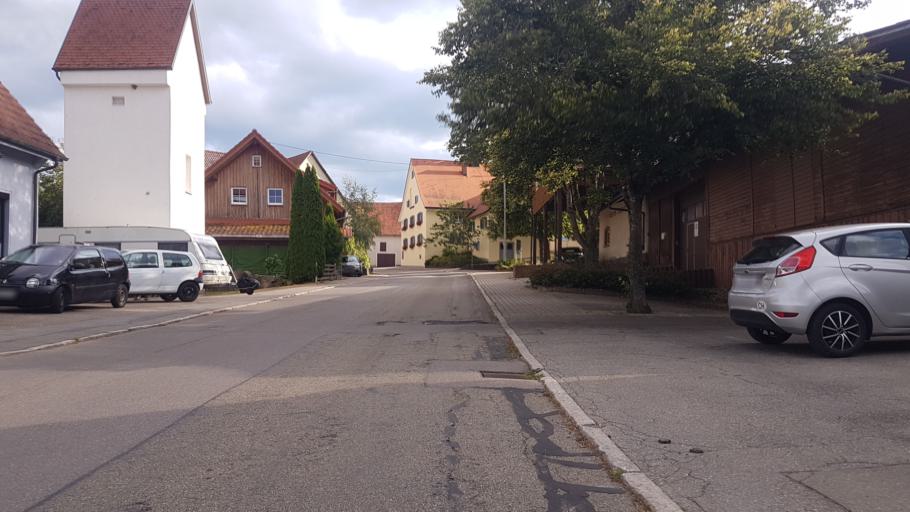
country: DE
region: Baden-Wuerttemberg
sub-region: Freiburg Region
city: Braunlingen
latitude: 48.0008
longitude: 8.4102
